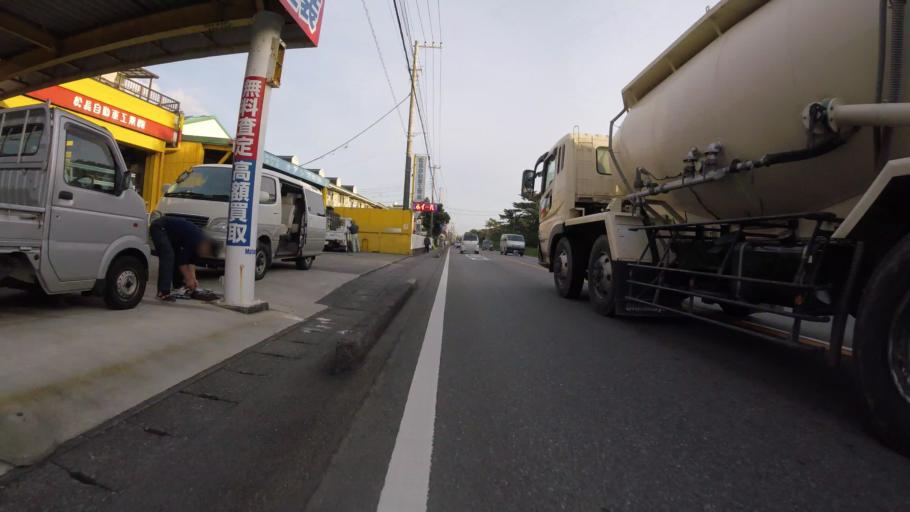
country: JP
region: Shizuoka
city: Numazu
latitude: 35.1136
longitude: 138.8205
